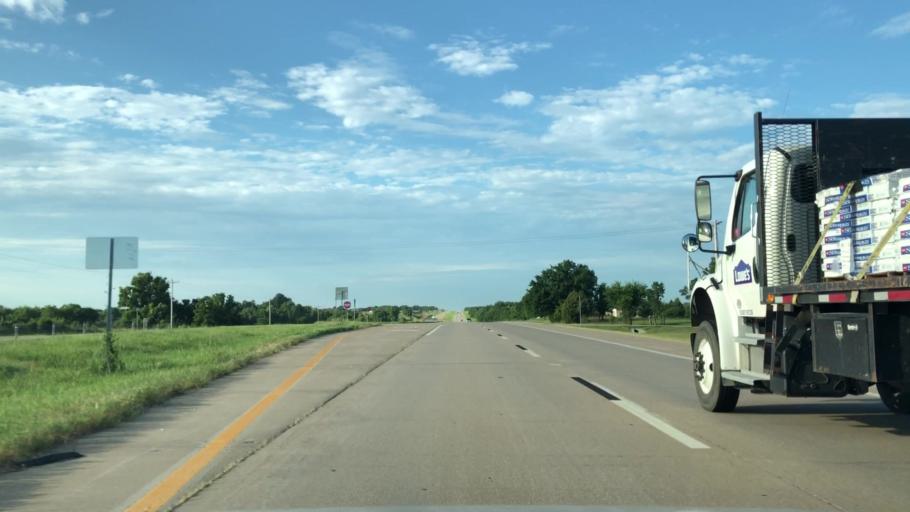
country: US
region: Oklahoma
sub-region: Osage County
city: Skiatook
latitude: 36.4459
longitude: -95.9211
